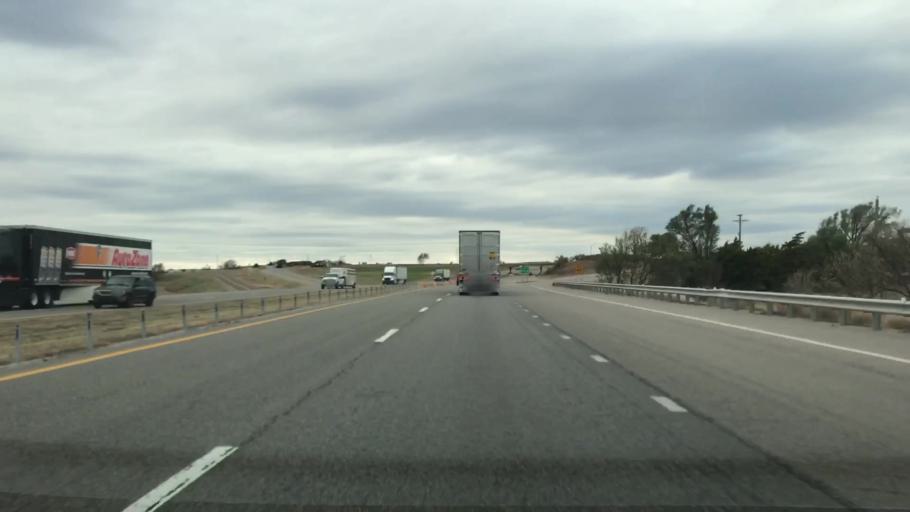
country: US
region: Oklahoma
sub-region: Washita County
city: Burns Flat
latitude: 35.4460
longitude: -99.1666
